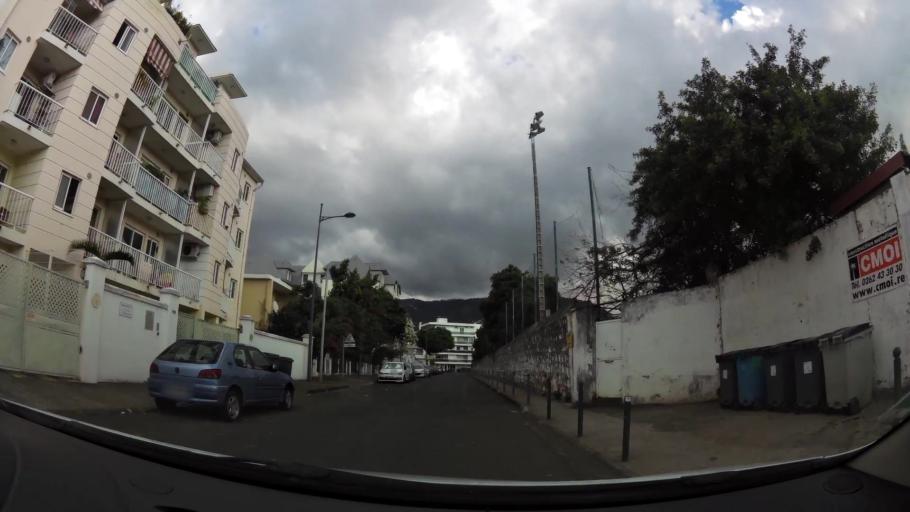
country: RE
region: Reunion
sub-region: Reunion
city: Saint-Denis
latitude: -20.8845
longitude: 55.4567
